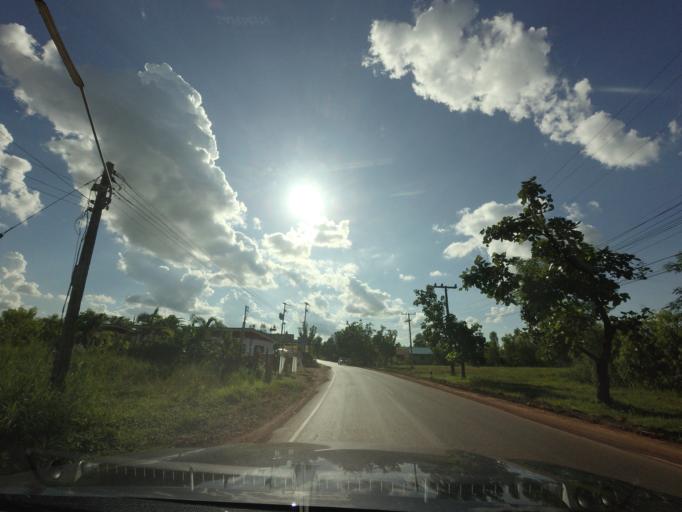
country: TH
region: Changwat Udon Thani
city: Ban Dung
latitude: 17.7450
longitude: 103.3182
